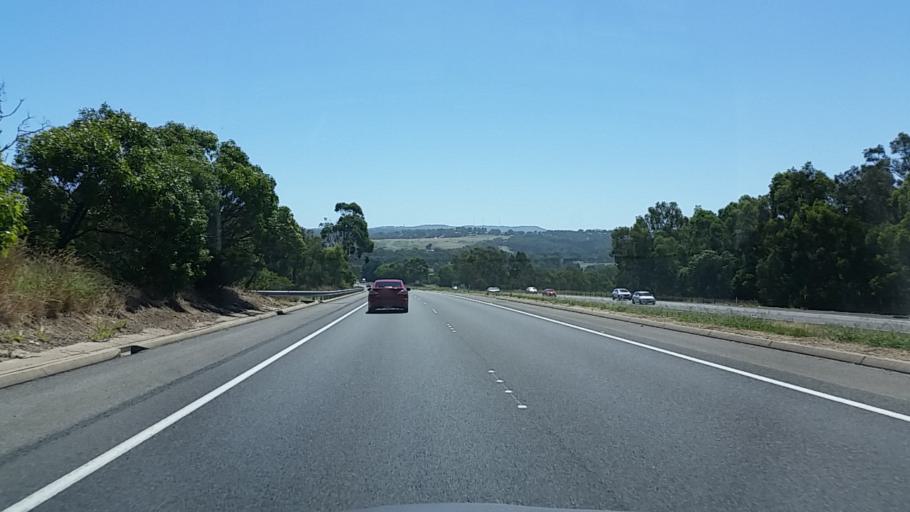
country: AU
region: South Australia
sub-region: Mount Barker
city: Hahndorf
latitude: -35.0285
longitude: 138.8002
